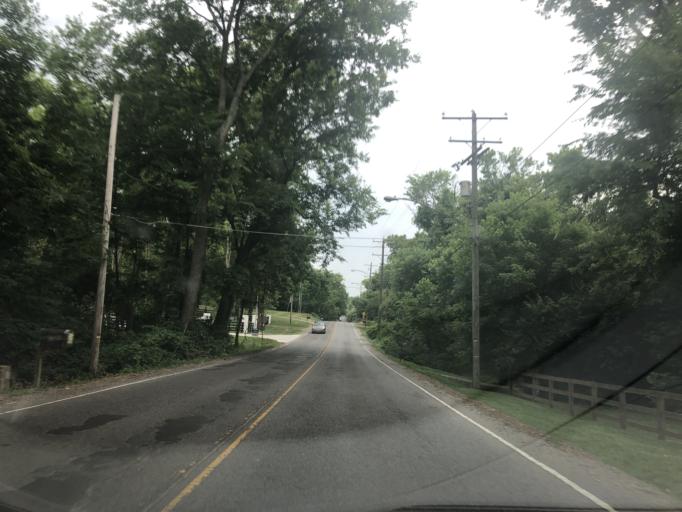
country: US
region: Tennessee
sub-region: Davidson County
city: Oak Hill
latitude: 36.0886
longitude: -86.7936
